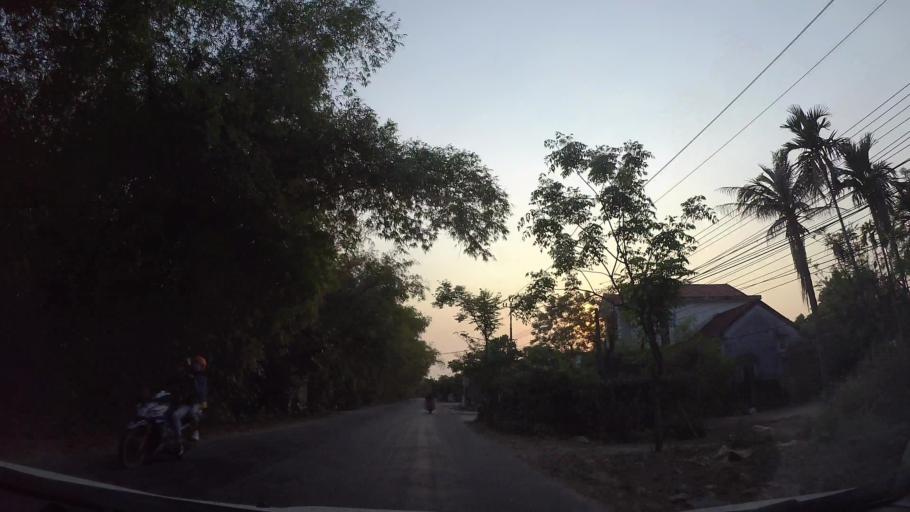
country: VN
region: Quang Nam
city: Quang Nam
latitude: 15.9498
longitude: 108.2282
